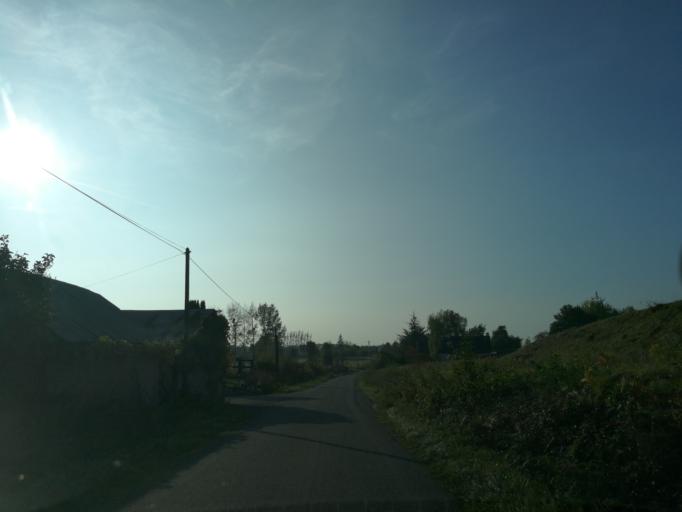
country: FR
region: Brittany
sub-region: Departement d'Ille-et-Vilaine
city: Pleumeleuc
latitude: 48.1764
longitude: -1.9147
